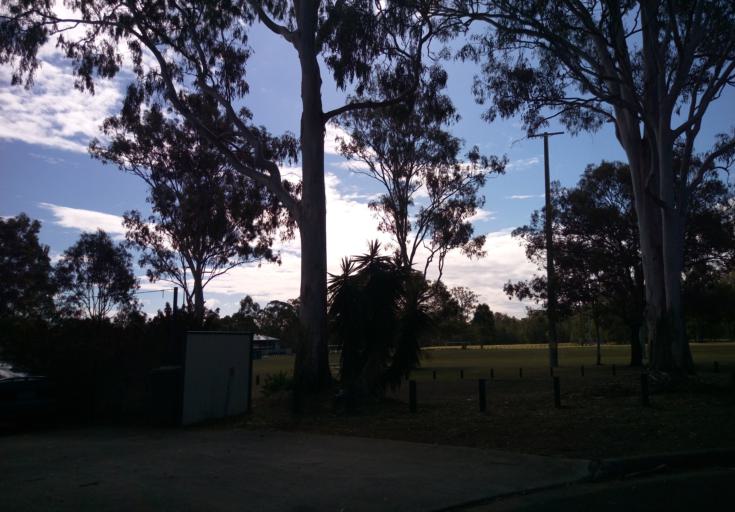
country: AU
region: Queensland
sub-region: Brisbane
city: Manly West
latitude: -27.4886
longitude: 153.2059
